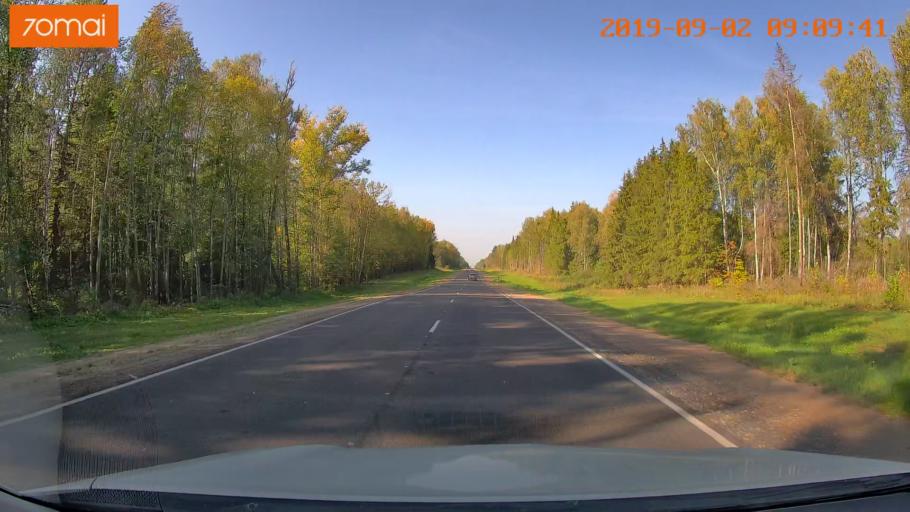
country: RU
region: Kaluga
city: Myatlevo
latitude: 54.8822
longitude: 35.6185
